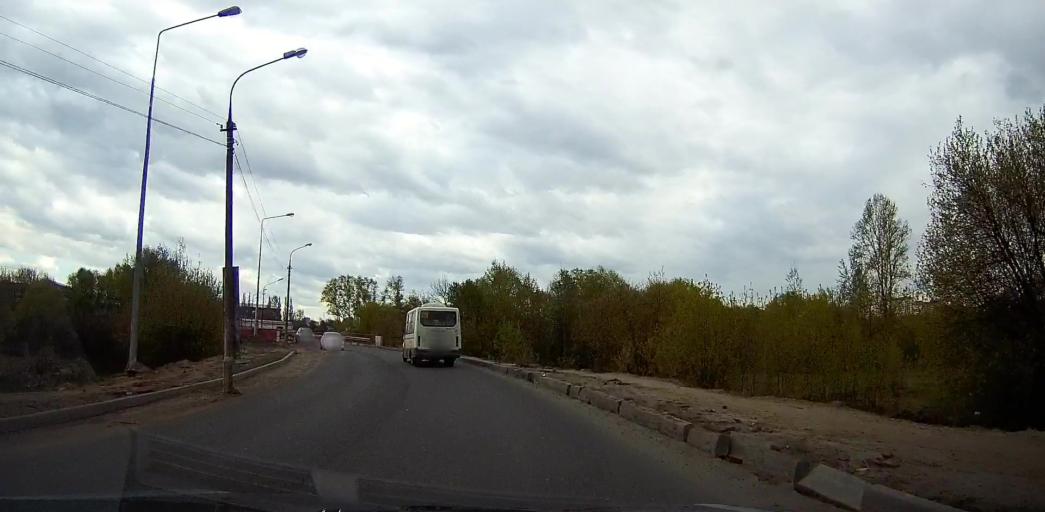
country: RU
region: Moskovskaya
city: Pavlovskiy Posad
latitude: 55.7809
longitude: 38.6878
